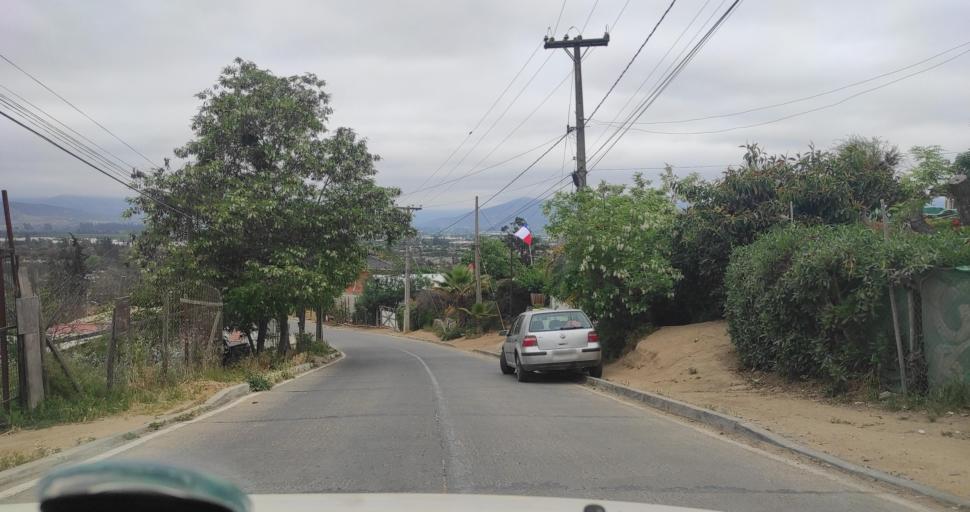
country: CL
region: Valparaiso
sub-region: Provincia de Marga Marga
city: Limache
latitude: -32.9913
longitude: -71.2264
